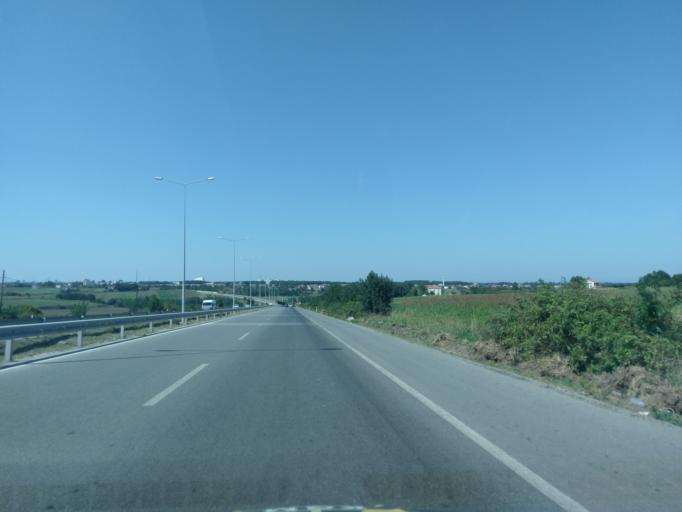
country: TR
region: Samsun
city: Bafra
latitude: 41.5325
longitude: 35.9504
